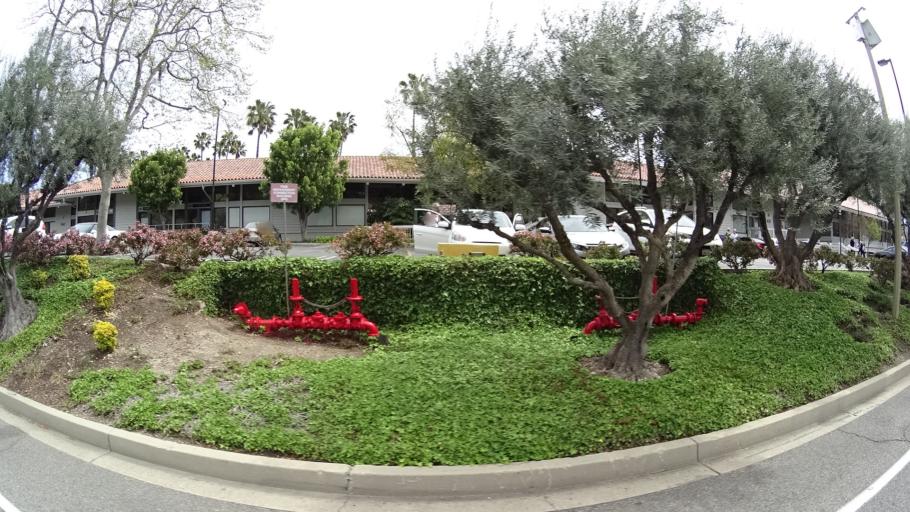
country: US
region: California
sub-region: Ventura County
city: Thousand Oaks
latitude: 34.1546
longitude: -118.8312
